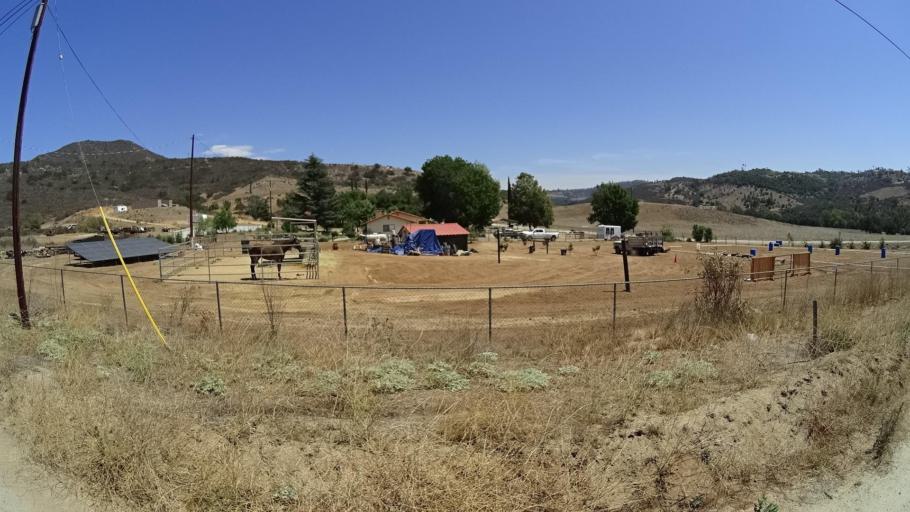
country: US
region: California
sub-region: San Diego County
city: Hidden Meadows
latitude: 33.2923
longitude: -117.0815
